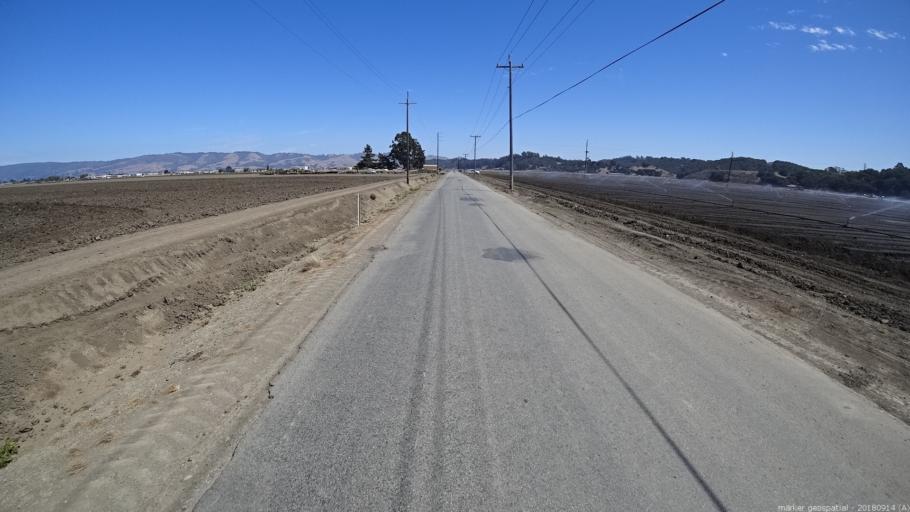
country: US
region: California
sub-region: Monterey County
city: Pajaro
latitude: 36.8843
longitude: -121.7569
